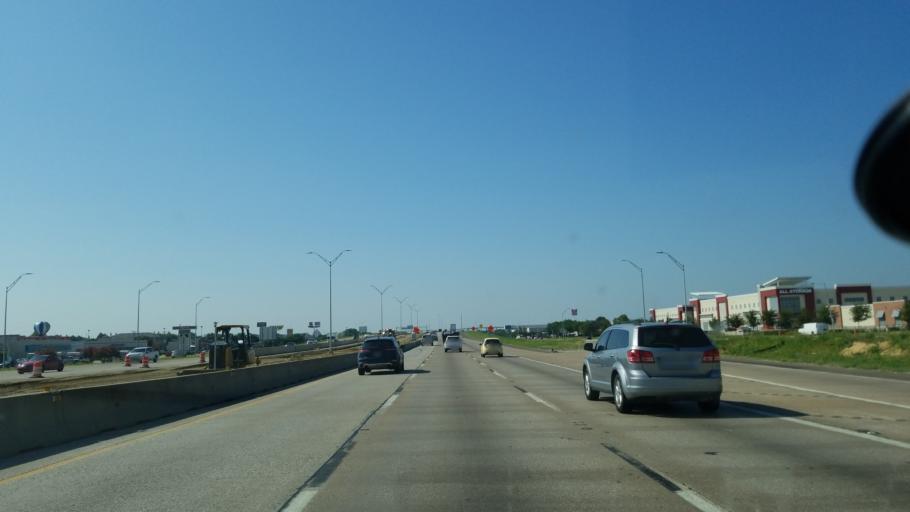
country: US
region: Texas
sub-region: Tarrant County
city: Arlington
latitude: 32.6969
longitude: -97.0631
